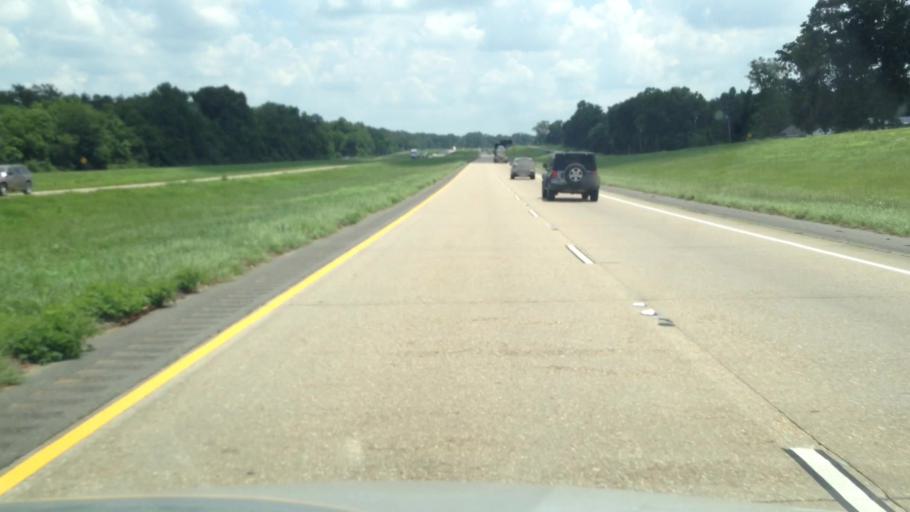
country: US
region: Louisiana
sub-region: Saint Landry Parish
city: Opelousas
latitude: 30.5599
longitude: -92.0520
